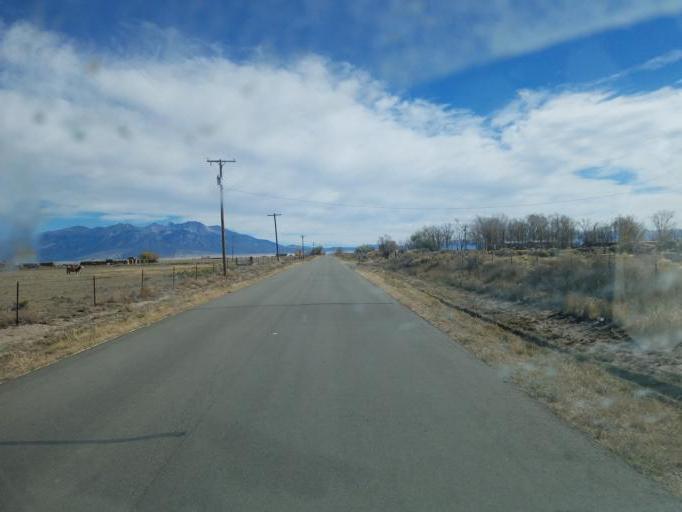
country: US
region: Colorado
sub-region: Alamosa County
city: Alamosa East
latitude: 37.5038
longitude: -105.8011
